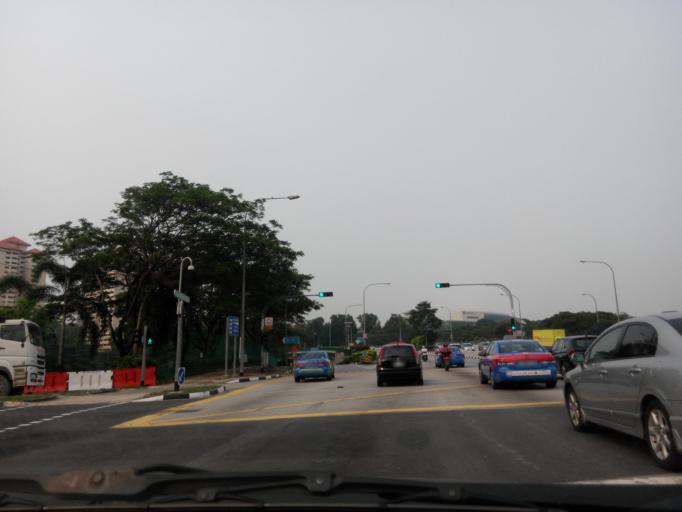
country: SG
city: Singapore
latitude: 1.2906
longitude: 103.7952
